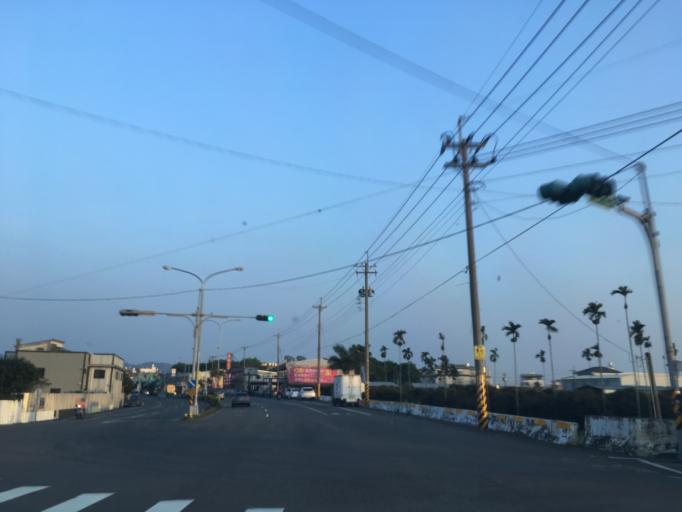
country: TW
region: Taiwan
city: Zhongxing New Village
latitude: 23.9928
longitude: 120.6665
